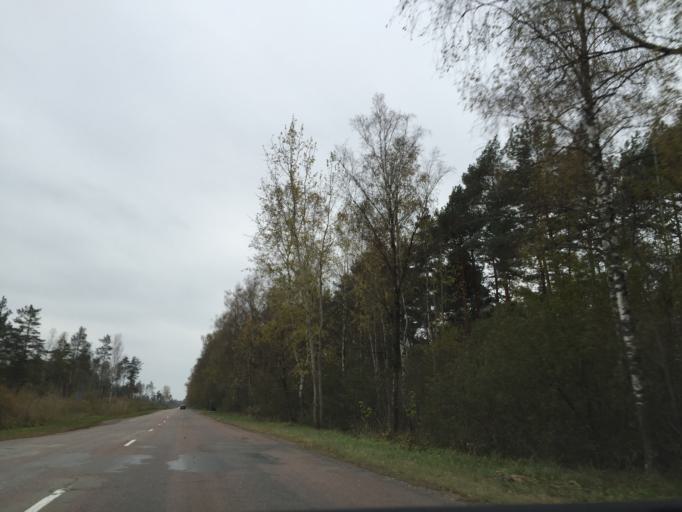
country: LV
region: Marupe
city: Marupe
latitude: 56.8706
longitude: 24.0635
